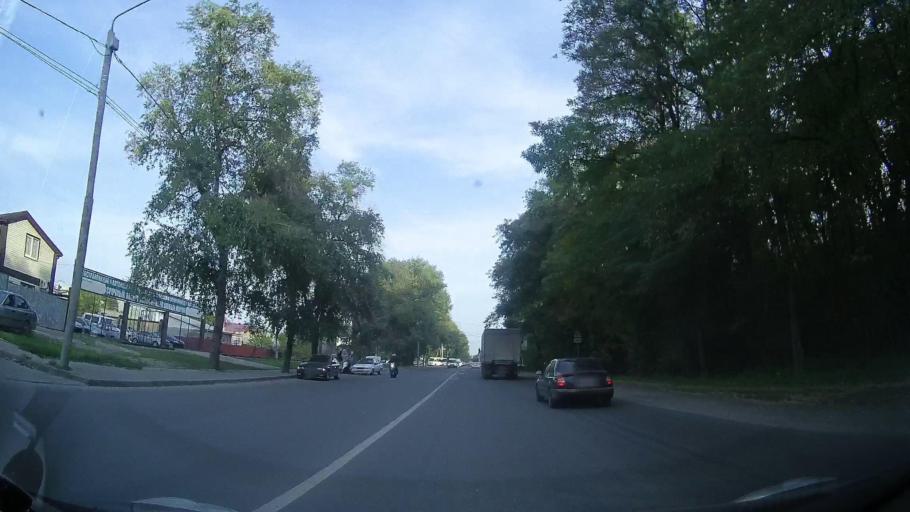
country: RU
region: Rostov
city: Imeni Chkalova
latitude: 47.2778
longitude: 39.8006
